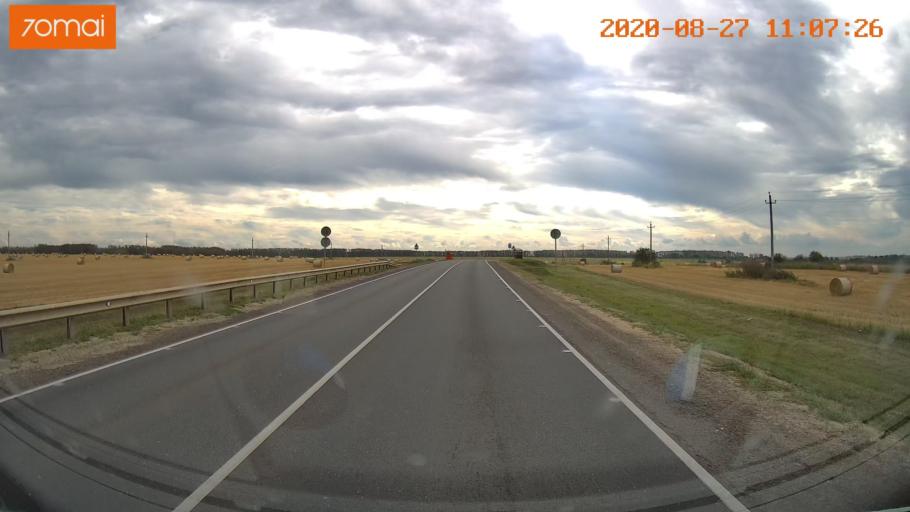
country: RU
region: Rjazan
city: Oktyabr'skiy
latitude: 54.1554
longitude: 38.6874
